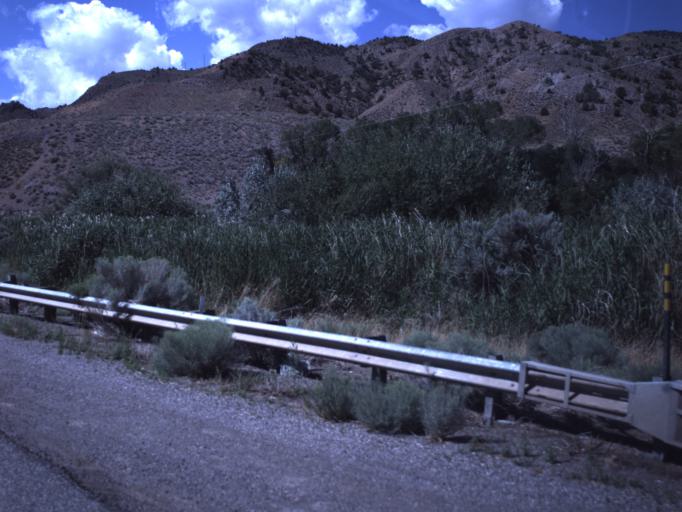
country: US
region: Utah
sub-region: Sevier County
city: Monroe
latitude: 38.5832
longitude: -112.2584
